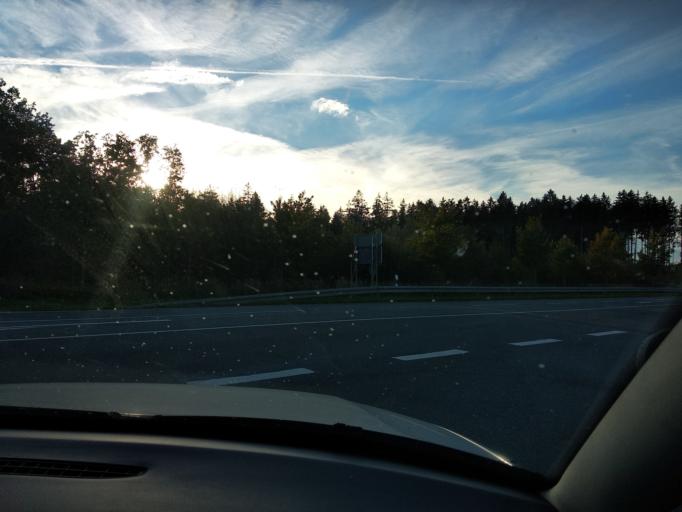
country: DE
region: Bavaria
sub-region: Upper Bavaria
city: Hohenbrunn
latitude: 48.0265
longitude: 11.6974
